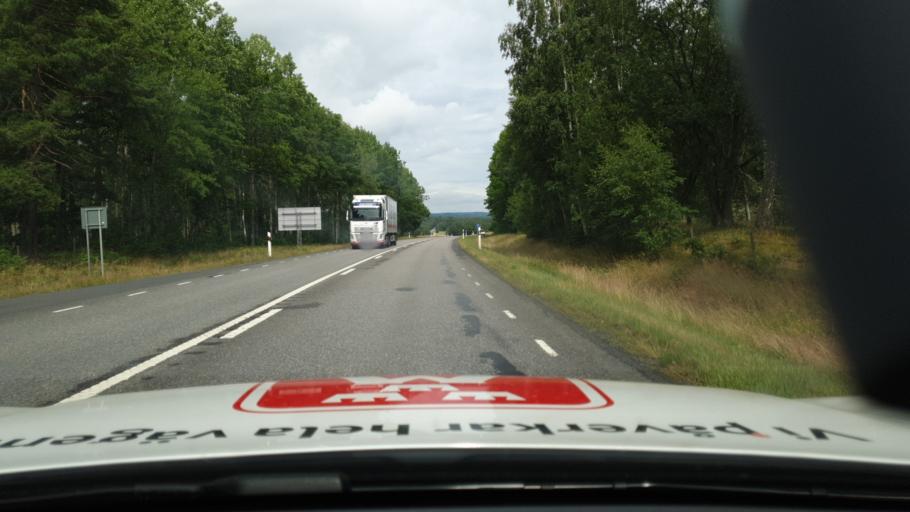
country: SE
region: Joenkoeping
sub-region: Habo Kommun
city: Habo
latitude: 57.9265
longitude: 14.0952
